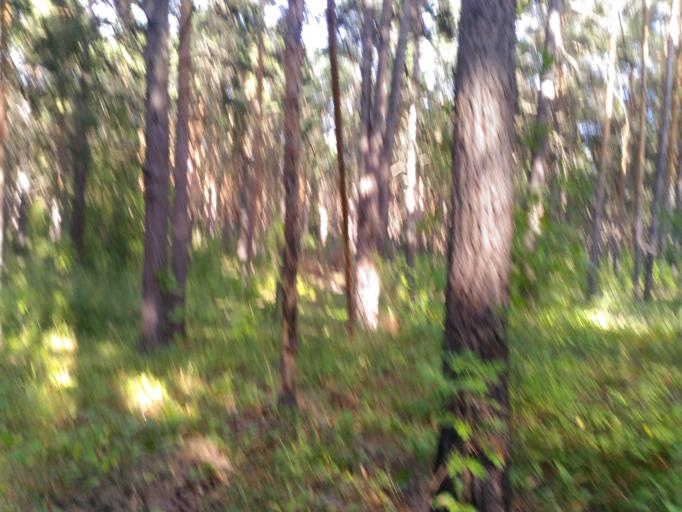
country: RU
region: Ulyanovsk
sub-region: Ulyanovskiy Rayon
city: Ulyanovsk
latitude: 54.3534
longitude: 48.5198
